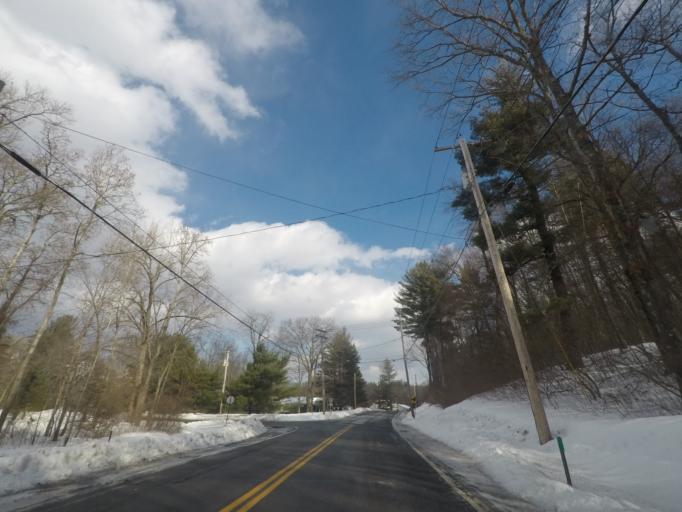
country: US
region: New York
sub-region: Albany County
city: Cohoes
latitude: 42.8083
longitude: -73.7577
